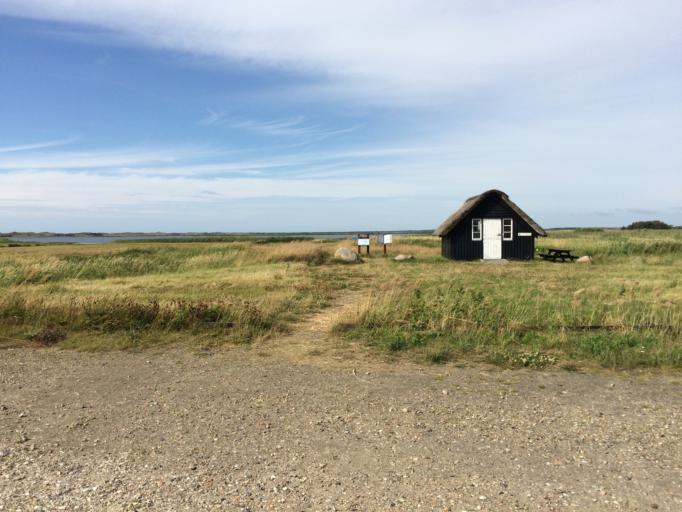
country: DK
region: Central Jutland
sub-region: Ringkobing-Skjern Kommune
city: Ringkobing
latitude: 56.2009
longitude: 8.1539
